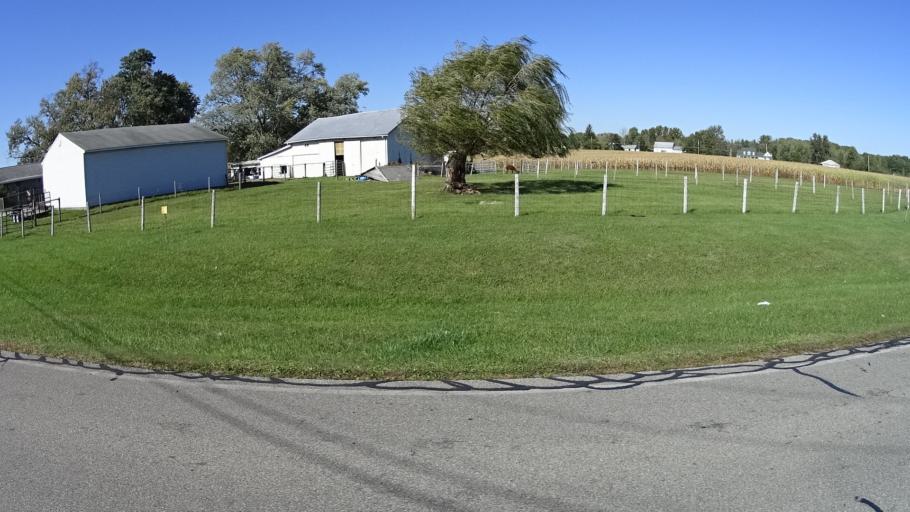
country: US
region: Ohio
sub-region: Lorain County
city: Oberlin
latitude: 41.2793
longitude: -82.1887
